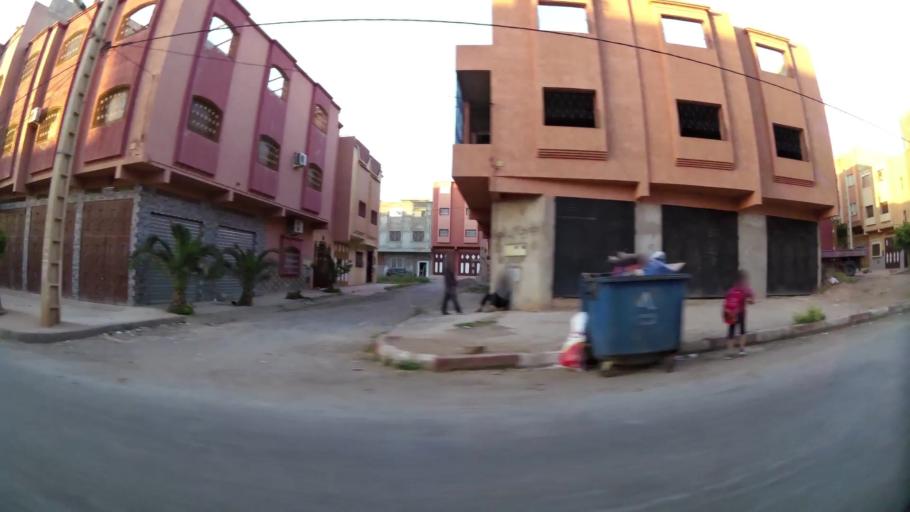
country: MA
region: Oriental
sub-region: Berkane-Taourirt
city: Berkane
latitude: 34.9126
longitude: -2.3186
